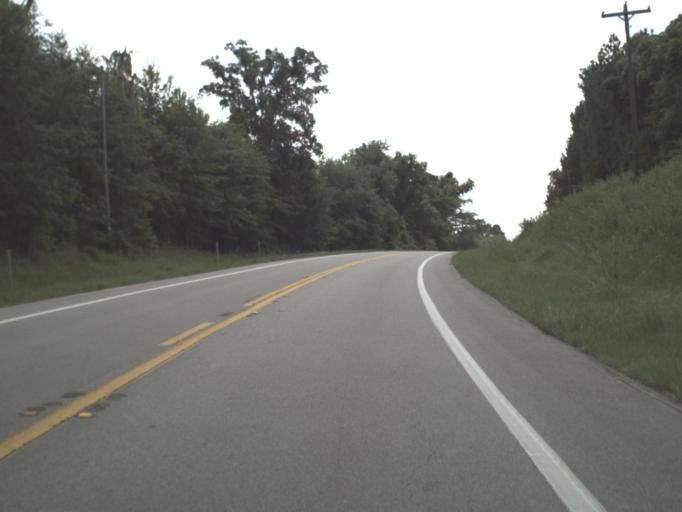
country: US
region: Florida
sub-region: Madison County
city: Madison
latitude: 30.5292
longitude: -83.4225
